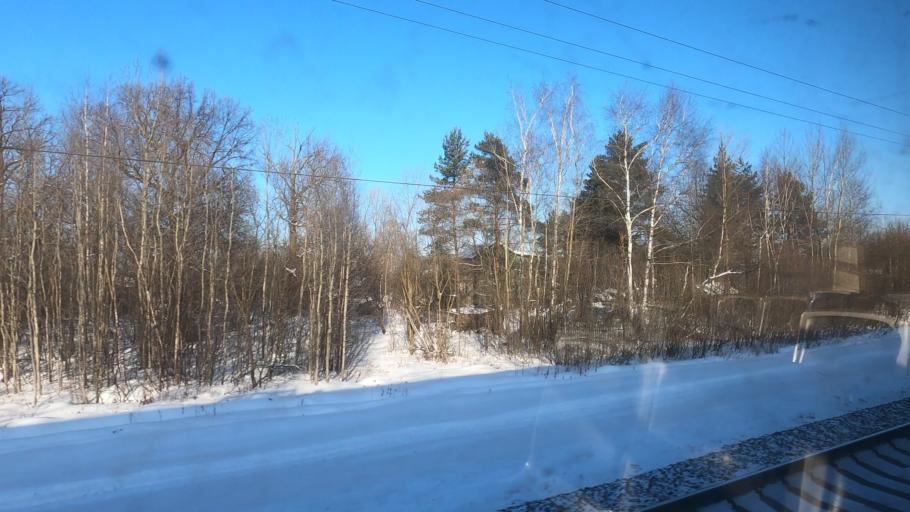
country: RU
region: Moskovskaya
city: Imeni Vorovskogo
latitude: 55.7216
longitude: 38.3162
